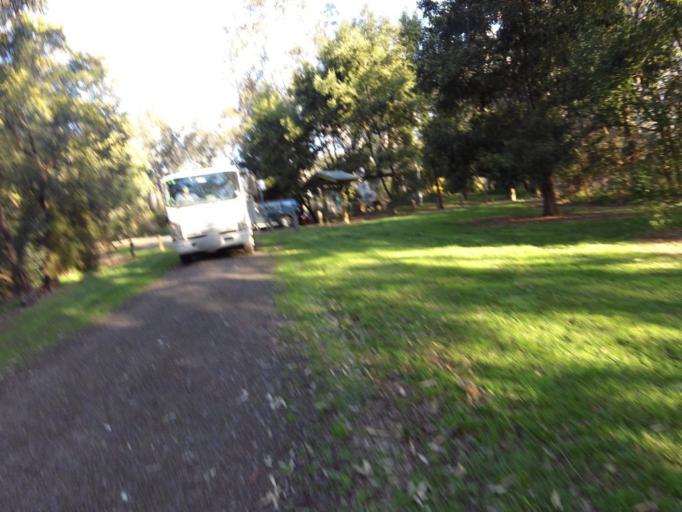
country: AU
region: Victoria
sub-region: Murrindindi
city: Alexandra
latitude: -37.2079
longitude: 145.4299
